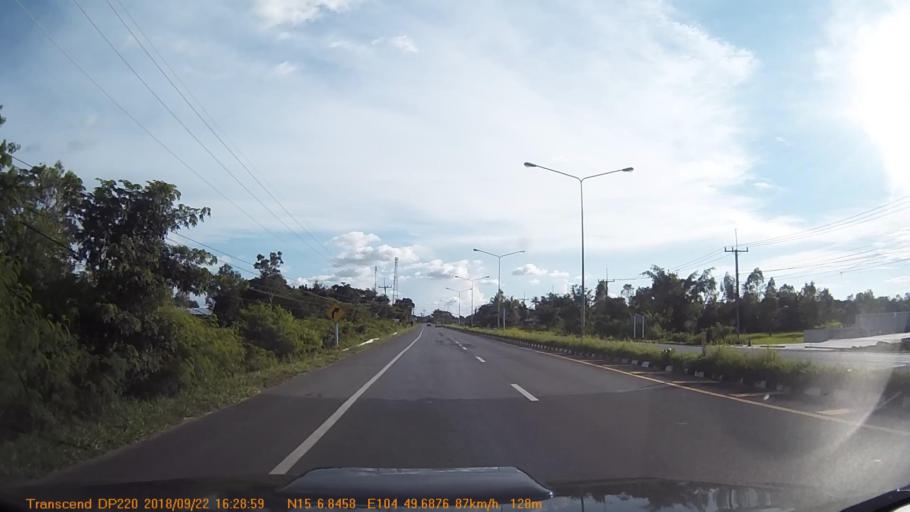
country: TH
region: Changwat Ubon Ratchathani
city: Warin Chamrap
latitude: 15.1141
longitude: 104.8281
